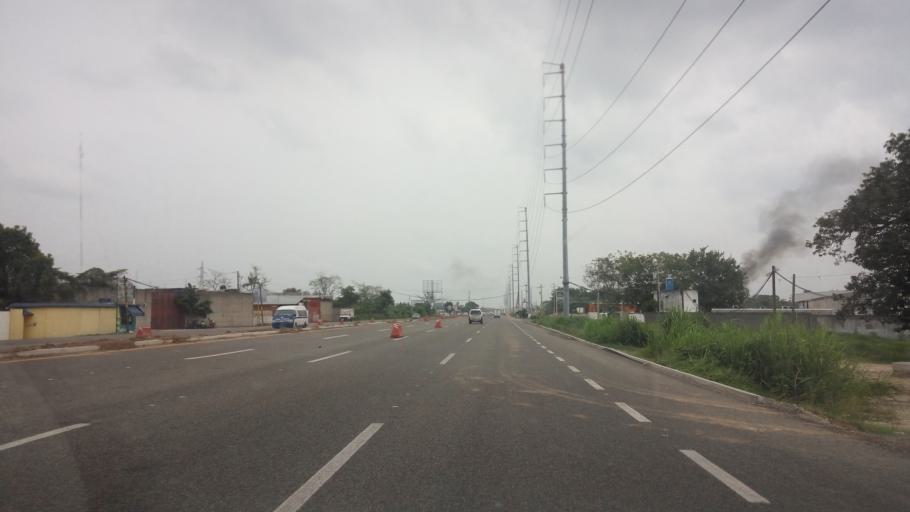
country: MX
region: Tabasco
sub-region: Centro
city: Anacleto Canabal 2da. Seccion
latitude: 17.9811
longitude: -93.0291
